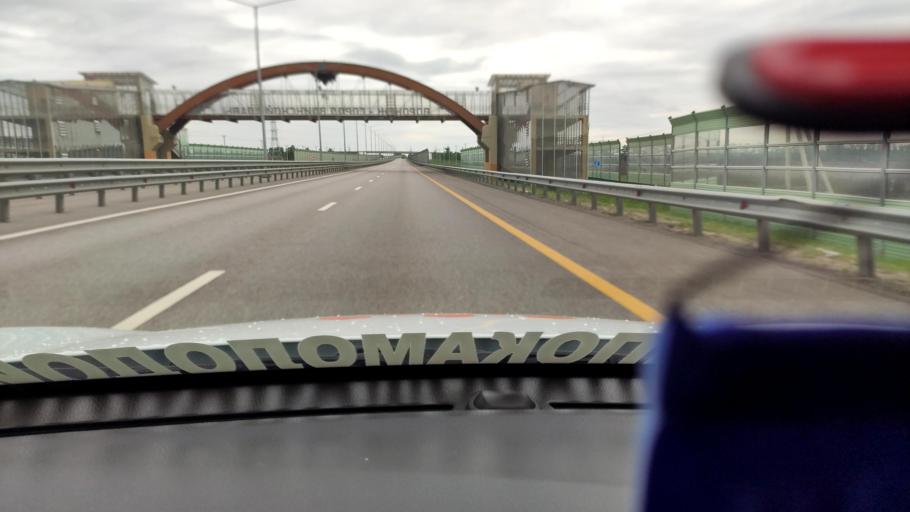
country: RU
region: Voronezj
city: Novaya Usman'
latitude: 51.6232
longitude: 39.3179
